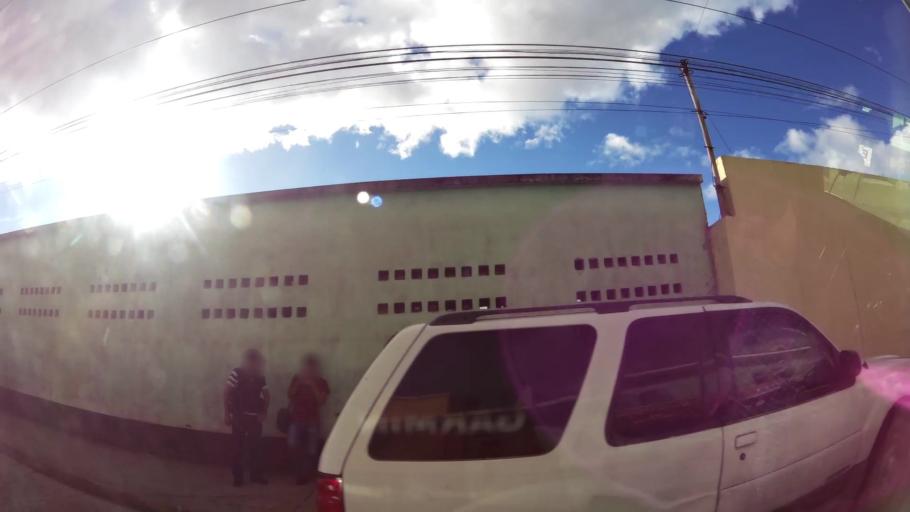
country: GT
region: Guatemala
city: Guatemala City
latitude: 14.6361
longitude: -90.5044
